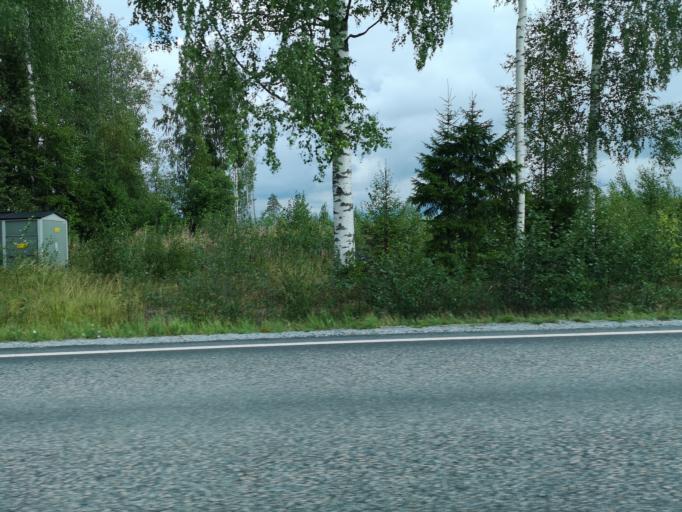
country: FI
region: Central Finland
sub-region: Jyvaeskylae
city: Hankasalmi
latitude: 62.3693
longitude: 26.4451
